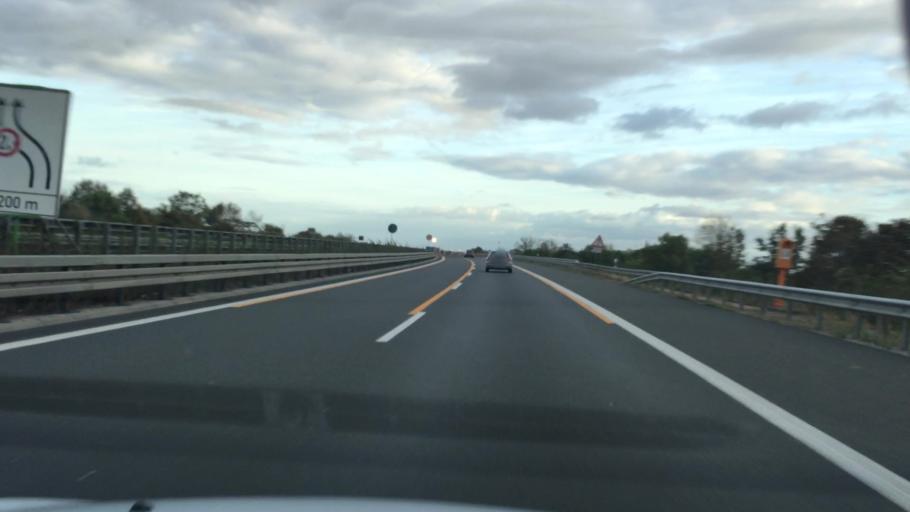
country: DE
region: Saxony-Anhalt
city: Plotzkau
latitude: 51.7303
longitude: 11.6720
